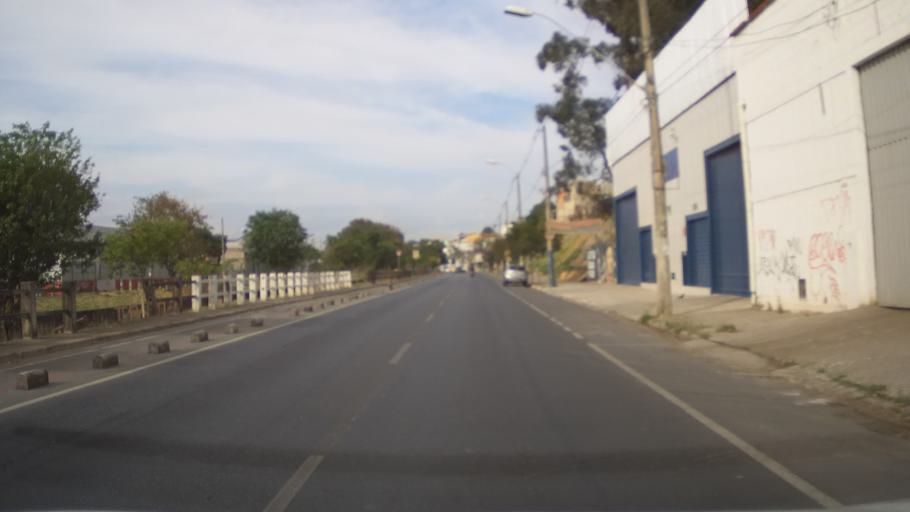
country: BR
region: Minas Gerais
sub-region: Contagem
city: Contagem
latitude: -19.8671
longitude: -44.0094
